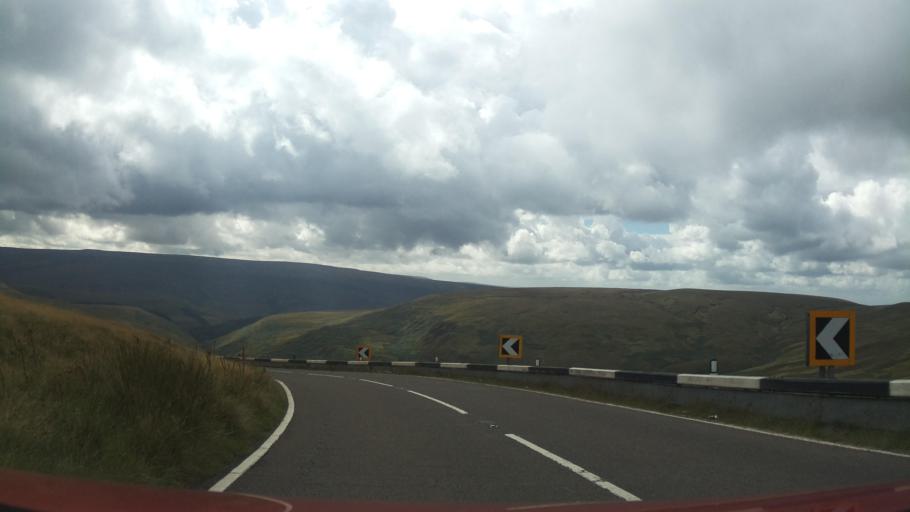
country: GB
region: England
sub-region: Kirklees
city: Meltham
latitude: 53.5285
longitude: -1.8576
